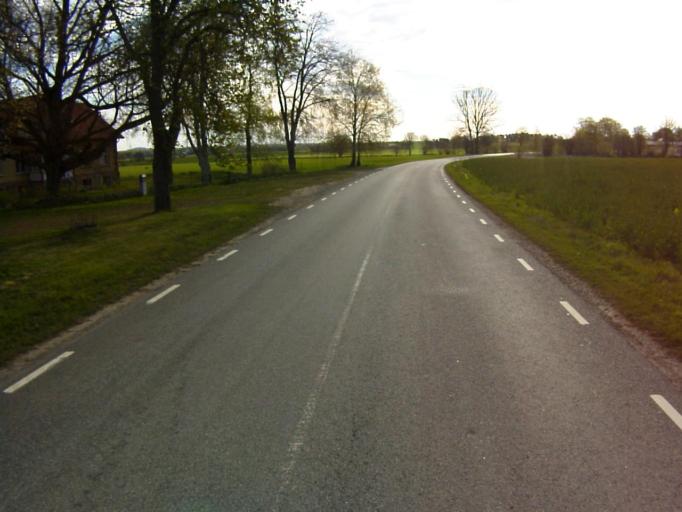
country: SE
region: Skane
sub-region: Kristianstads Kommun
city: Norra Asum
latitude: 55.9929
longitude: 14.1254
